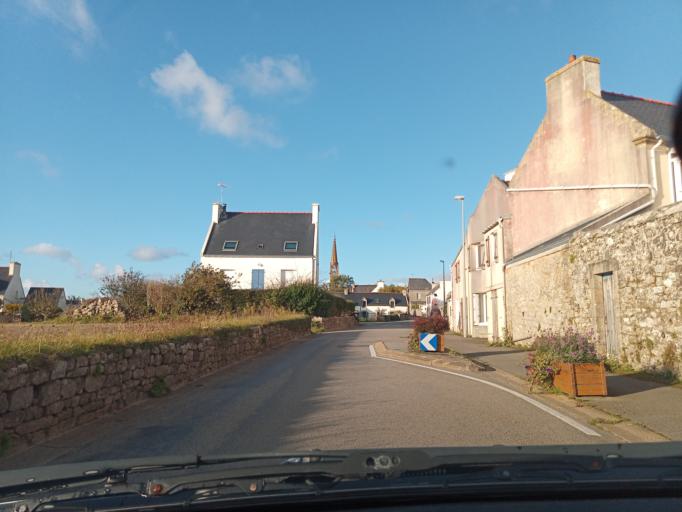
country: FR
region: Brittany
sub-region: Departement du Finistere
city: Esquibien
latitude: 48.0224
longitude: -4.5634
